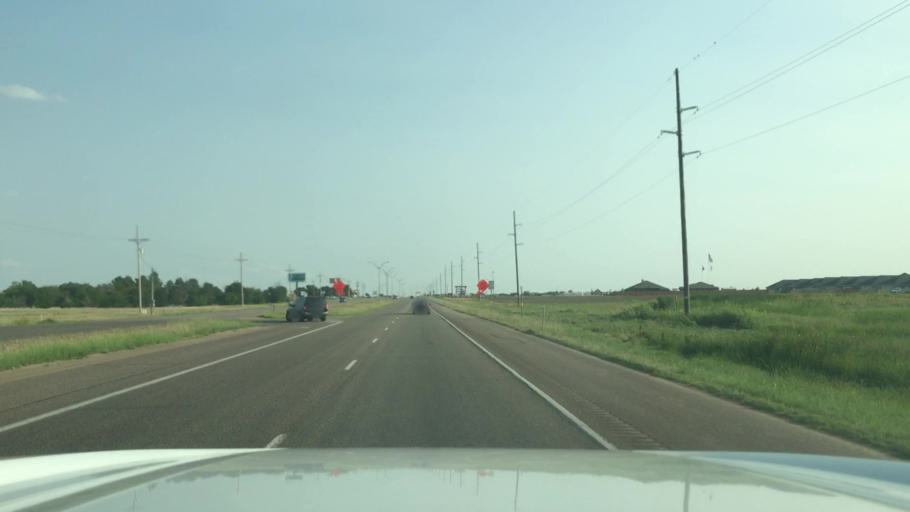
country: US
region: Texas
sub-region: Potter County
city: Bushland
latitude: 35.1302
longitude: -101.9382
